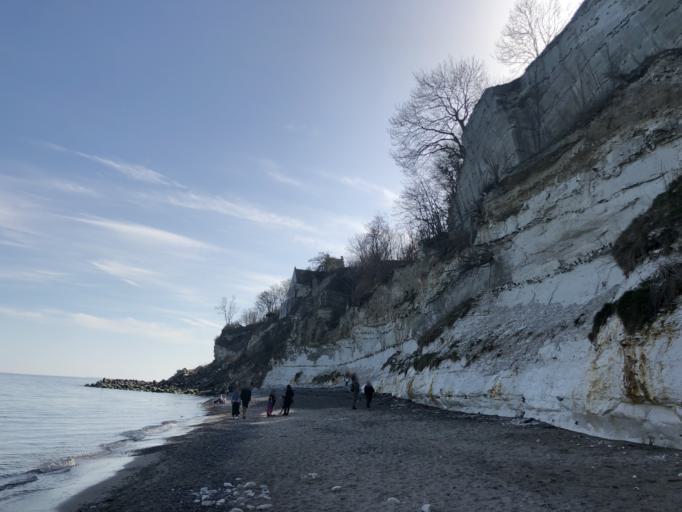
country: DK
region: Zealand
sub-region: Stevns Kommune
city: Store Heddinge
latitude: 55.2805
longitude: 12.4469
